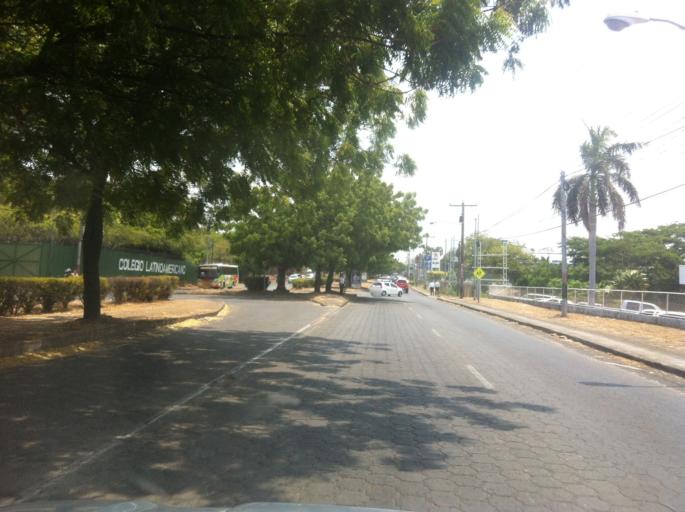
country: NI
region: Managua
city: Managua
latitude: 12.1127
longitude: -86.2592
